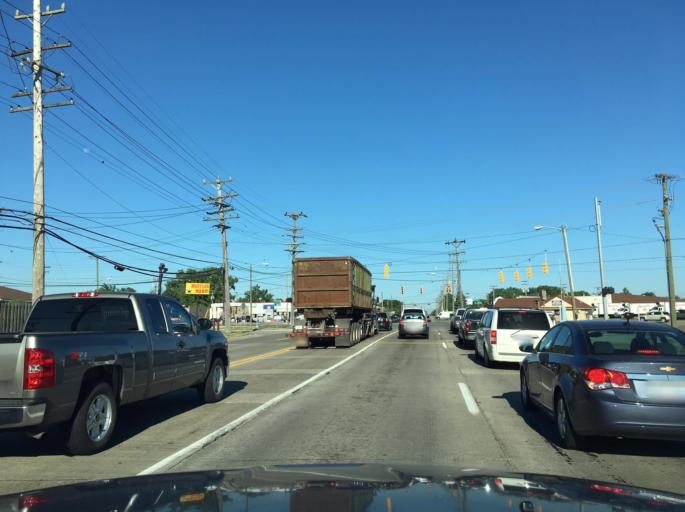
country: US
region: Michigan
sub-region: Macomb County
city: Fraser
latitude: 42.5393
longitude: -82.9341
